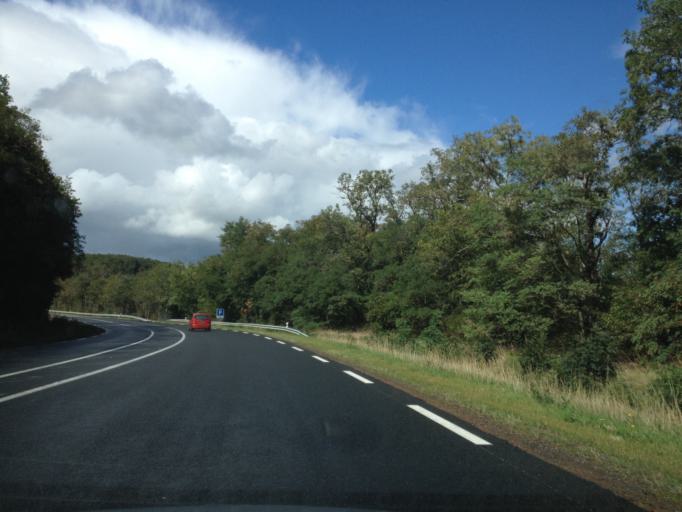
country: FR
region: Rhone-Alpes
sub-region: Departement du Rhone
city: Amplepuis
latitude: 45.9361
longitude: 4.2997
